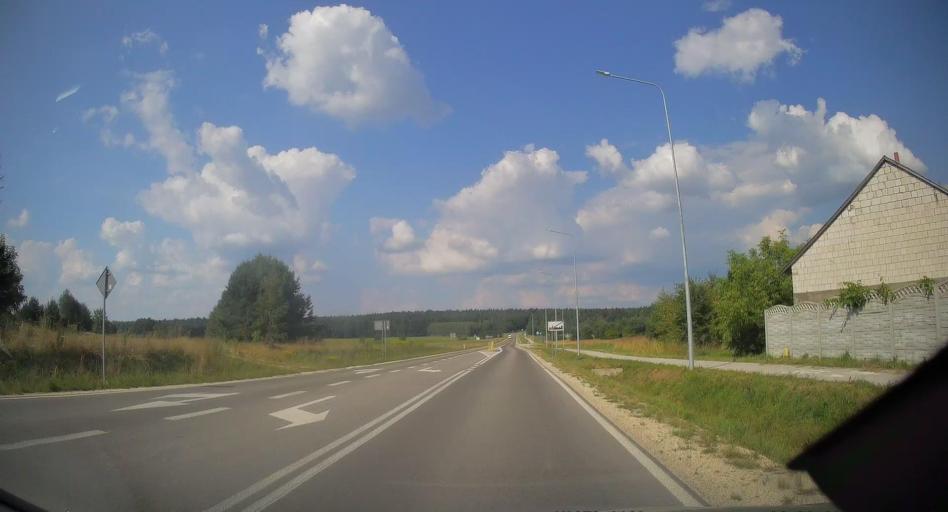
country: PL
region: Swietokrzyskie
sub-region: Powiat kielecki
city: Lopuszno
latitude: 50.9996
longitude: 20.2695
